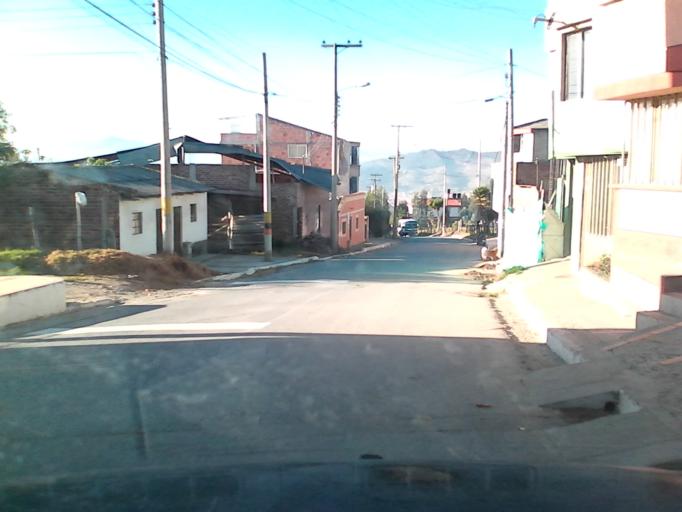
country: CO
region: Boyaca
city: Duitama
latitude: 5.8475
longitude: -73.0359
